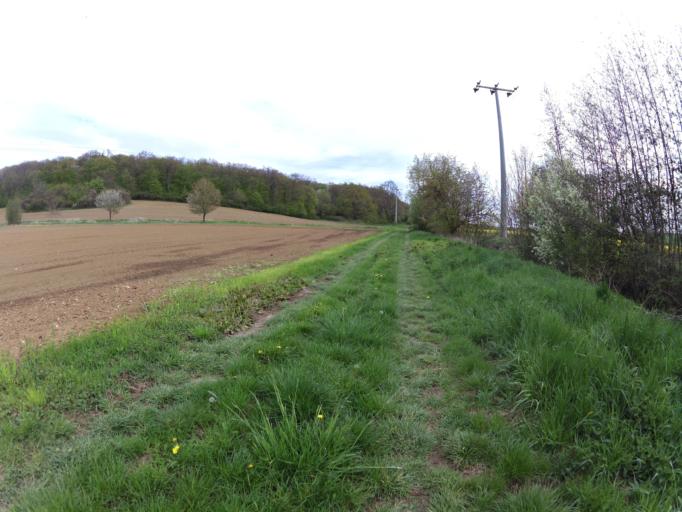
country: DE
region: Bavaria
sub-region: Regierungsbezirk Unterfranken
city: Prosselsheim
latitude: 49.8544
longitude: 10.1420
